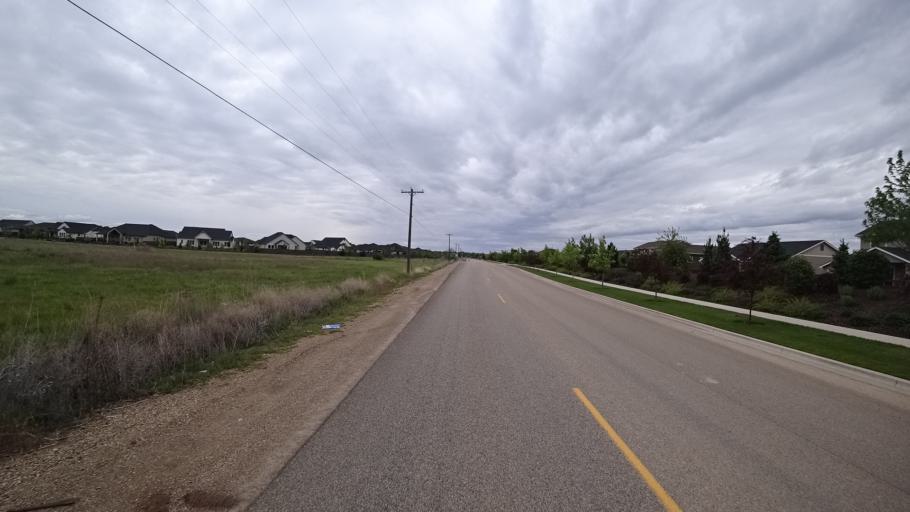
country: US
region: Idaho
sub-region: Ada County
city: Eagle
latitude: 43.7113
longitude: -116.4235
